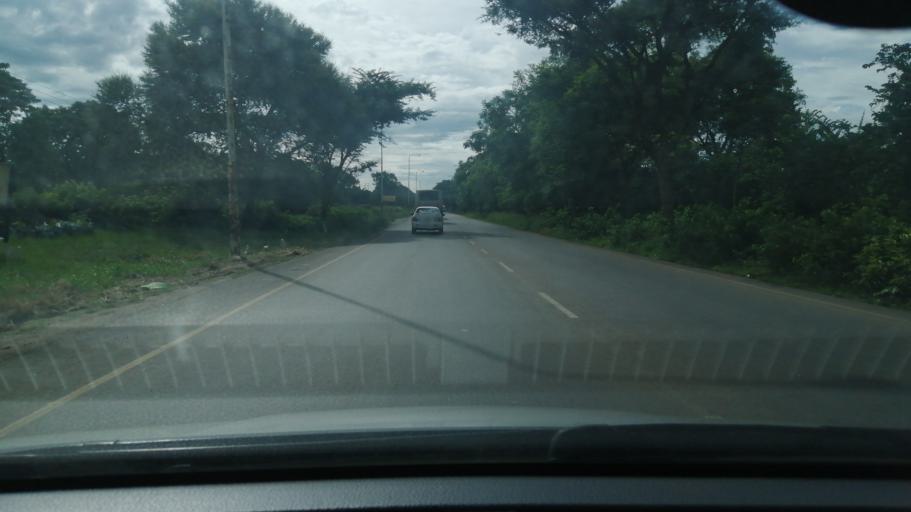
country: ZW
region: Harare
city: Harare
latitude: -17.7643
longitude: 30.9933
